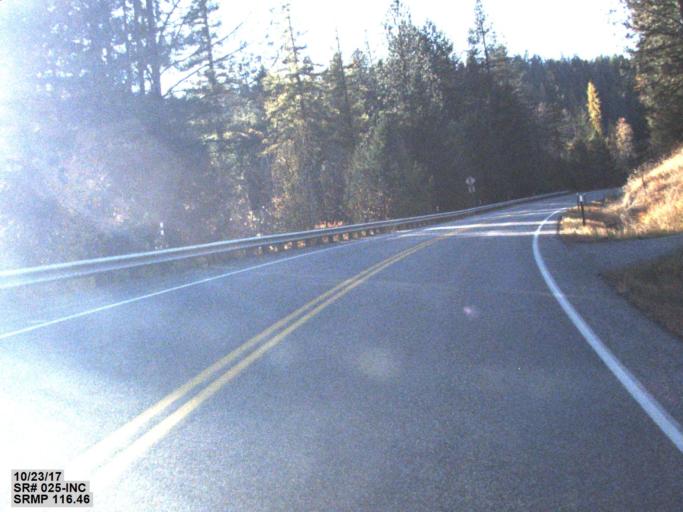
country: CA
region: British Columbia
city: Rossland
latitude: 48.9439
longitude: -117.7869
